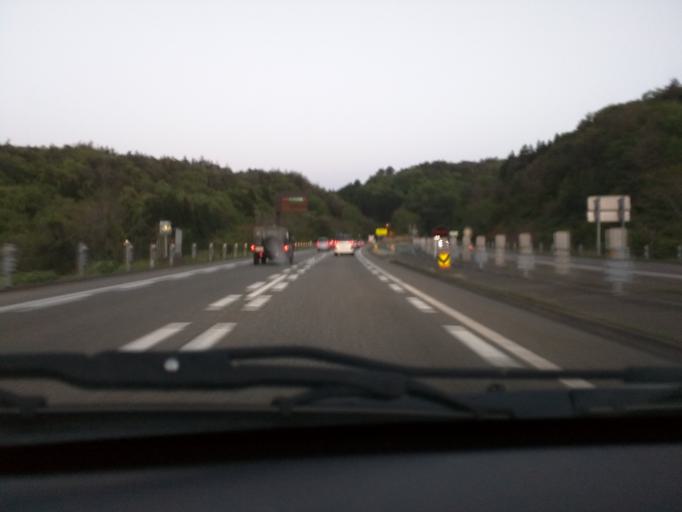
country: JP
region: Niigata
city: Kashiwazaki
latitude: 37.3458
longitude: 138.5123
